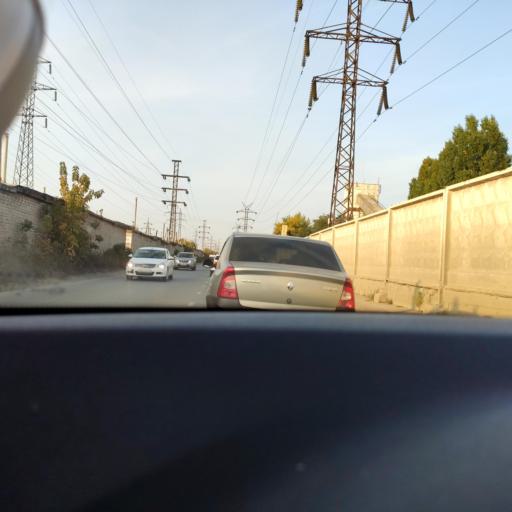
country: RU
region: Samara
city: Petra-Dubrava
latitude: 53.2485
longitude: 50.2935
